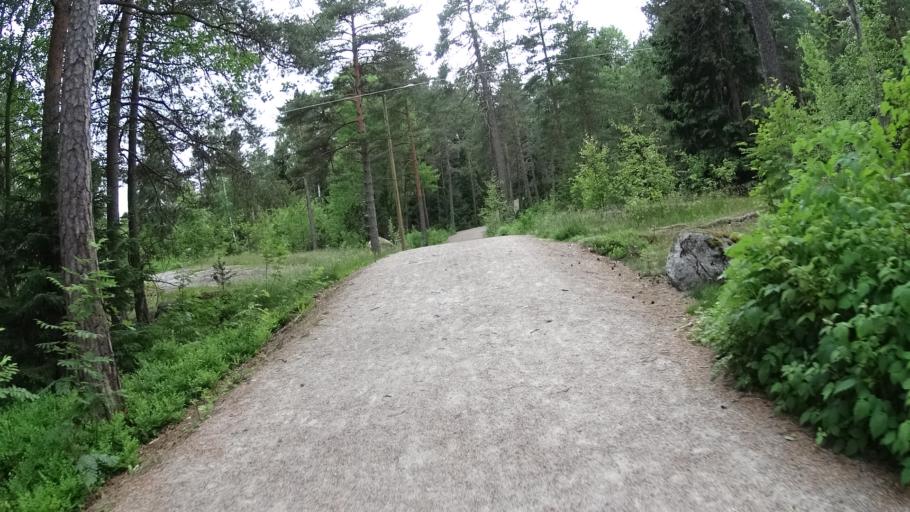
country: FI
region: Uusimaa
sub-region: Helsinki
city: Kilo
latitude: 60.1942
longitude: 24.7612
